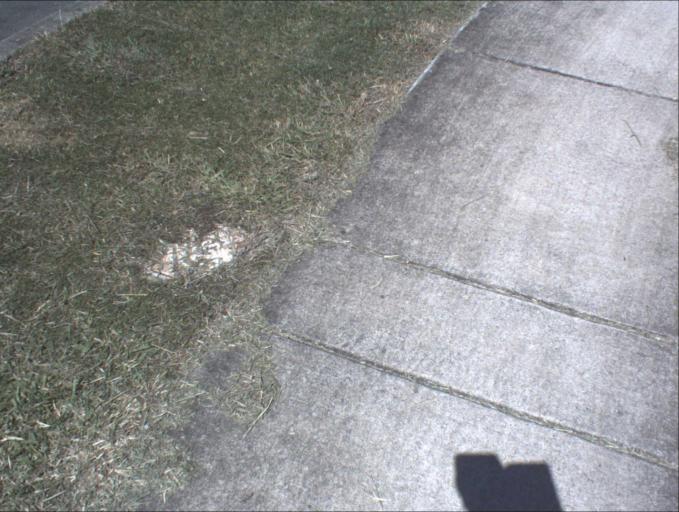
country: AU
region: Queensland
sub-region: Gold Coast
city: Yatala
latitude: -27.7054
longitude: 153.2281
